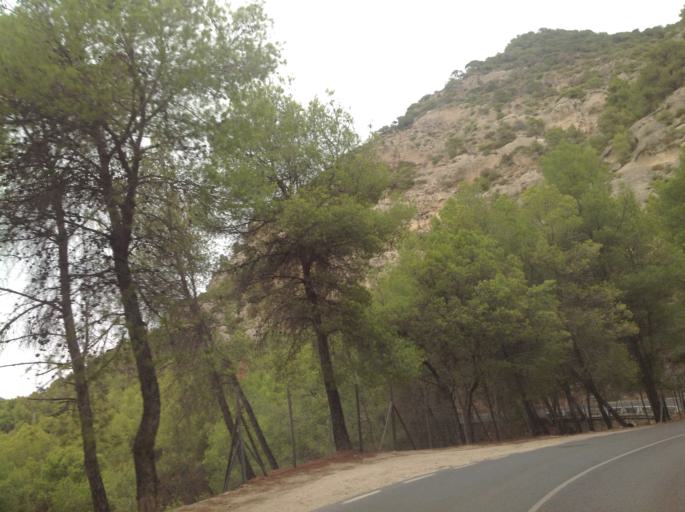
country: ES
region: Andalusia
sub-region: Provincia de Malaga
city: Ardales
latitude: 36.9211
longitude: -4.8027
